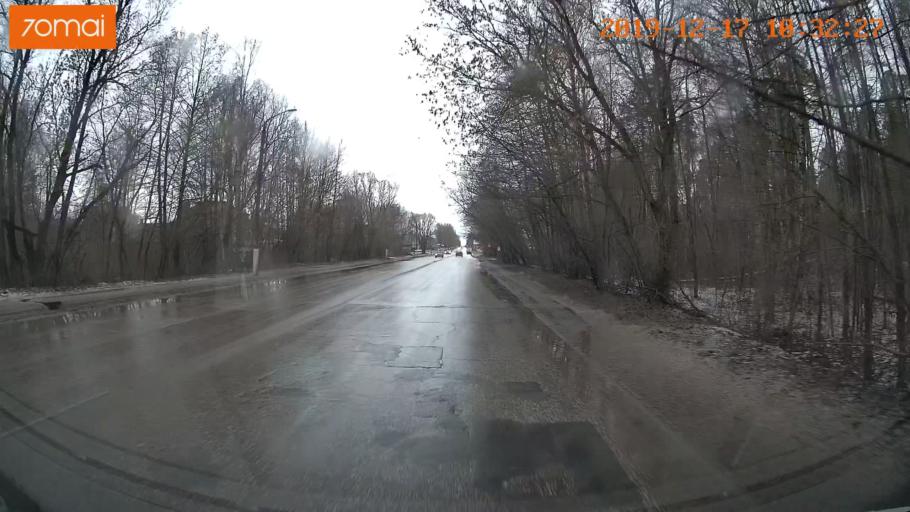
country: RU
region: Vladimir
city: Gus'-Khrustal'nyy
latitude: 55.6286
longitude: 40.6886
